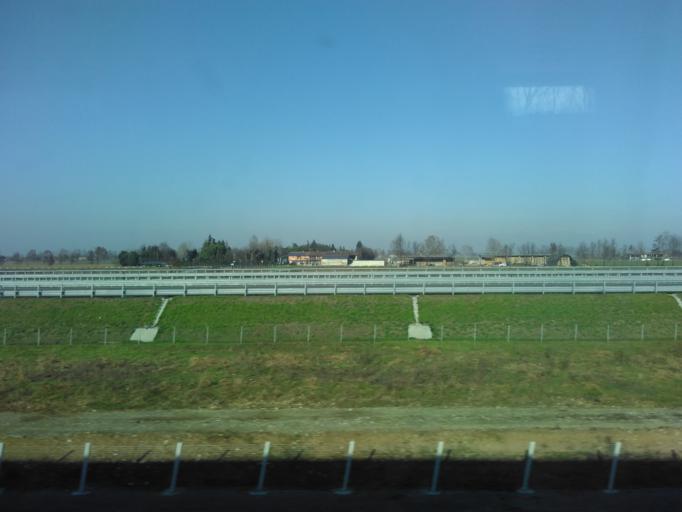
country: IT
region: Lombardy
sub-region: Provincia di Bergamo
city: Antegnate
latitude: 45.4928
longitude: 9.7929
